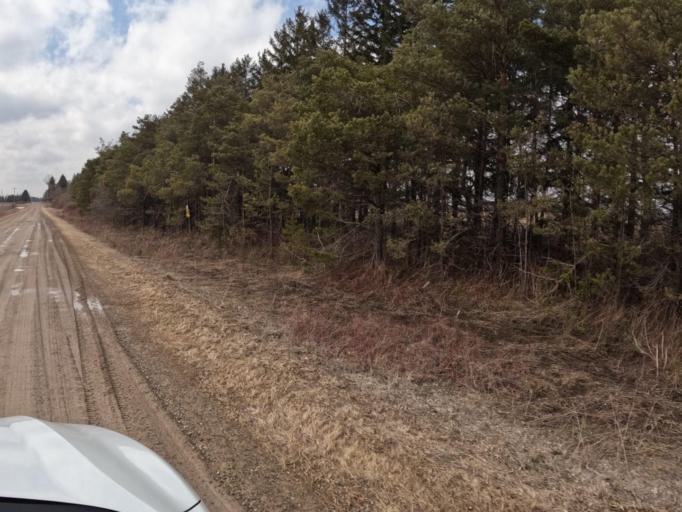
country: CA
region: Ontario
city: Shelburne
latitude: 44.0284
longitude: -80.2590
